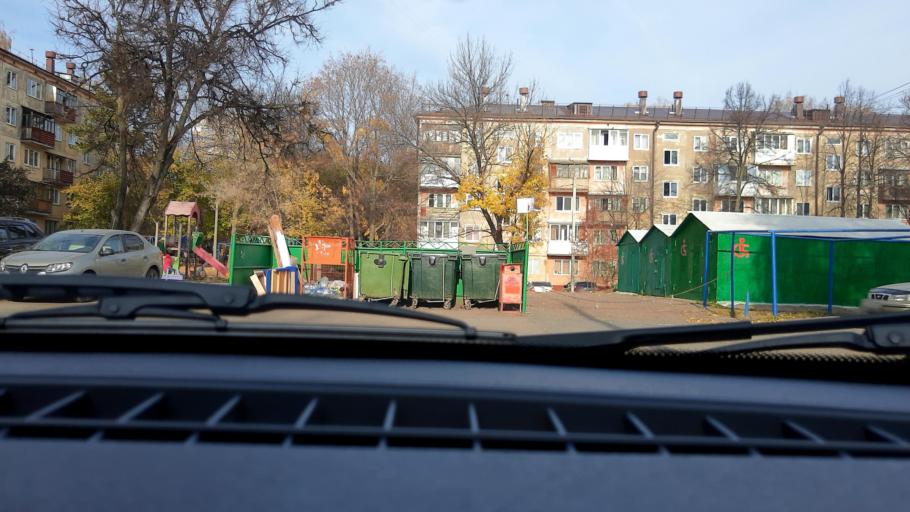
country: RU
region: Bashkortostan
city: Ufa
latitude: 54.7578
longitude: 56.0028
